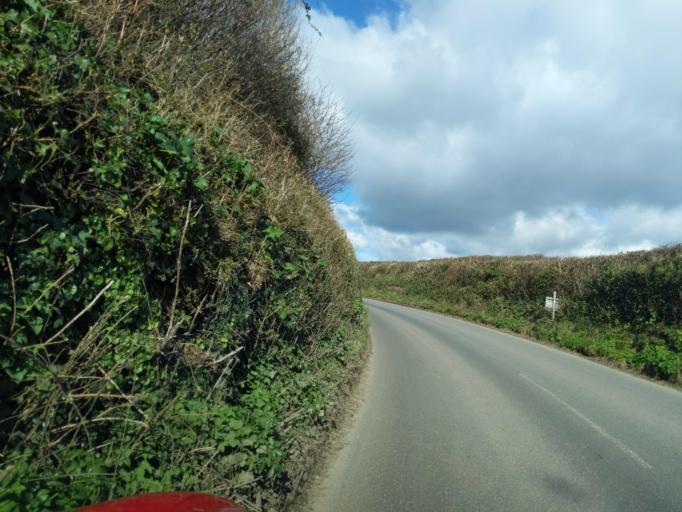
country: GB
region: England
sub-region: Devon
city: Kingsbridge
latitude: 50.2904
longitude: -3.7699
